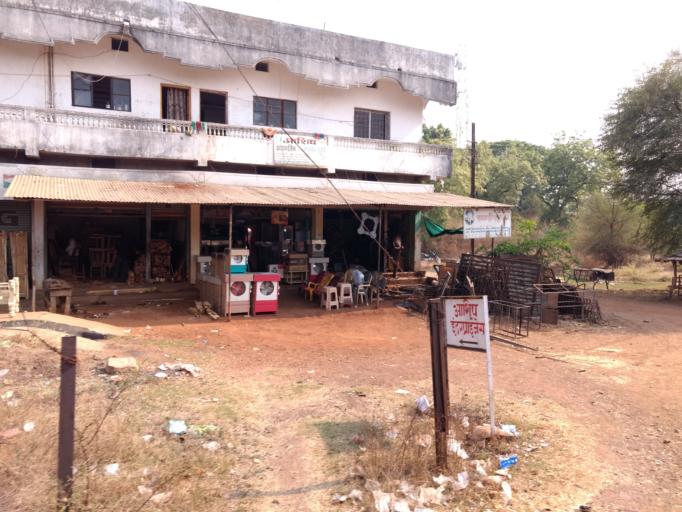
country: IN
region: Maharashtra
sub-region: Bhandara
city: Pauni
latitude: 20.5825
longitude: 79.6905
